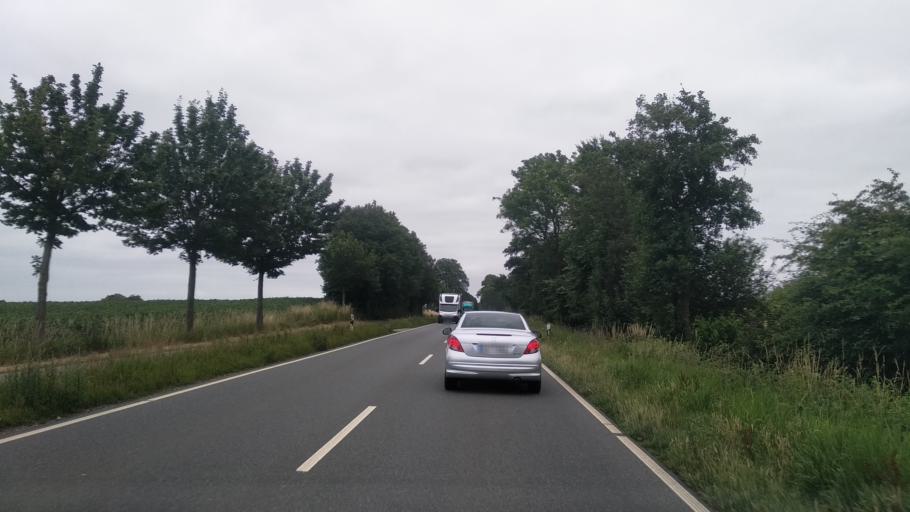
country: DE
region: Schleswig-Holstein
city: Ringsberg
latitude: 54.8028
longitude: 9.6124
